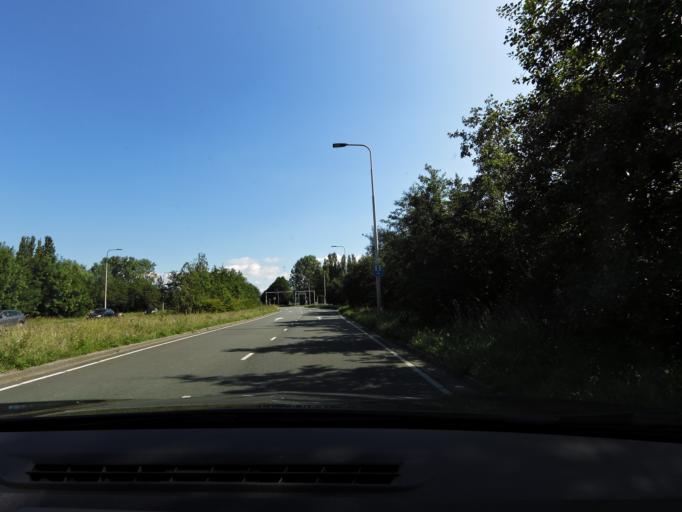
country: NL
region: North Holland
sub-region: Gemeente Amstelveen
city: Amstelveen
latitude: 52.2870
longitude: 4.8331
